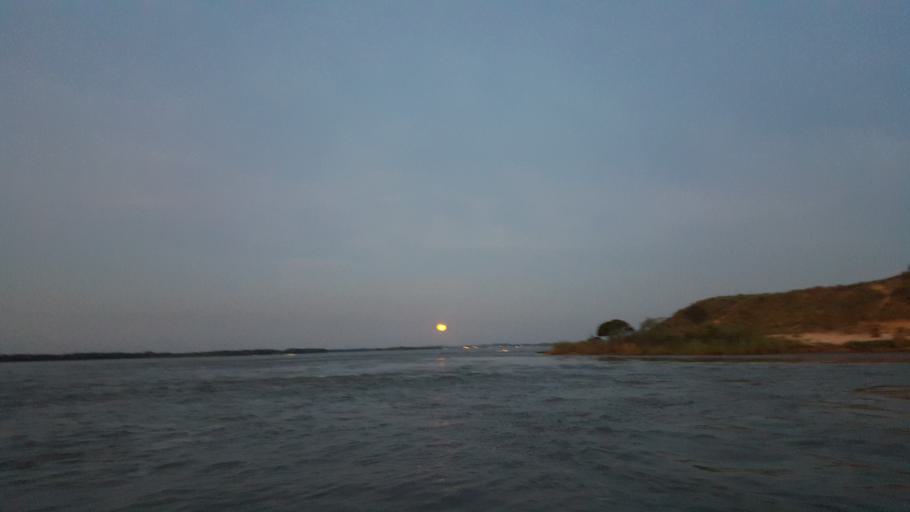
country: AR
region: Corrientes
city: Ituzaingo
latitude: -27.5887
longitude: -56.7951
